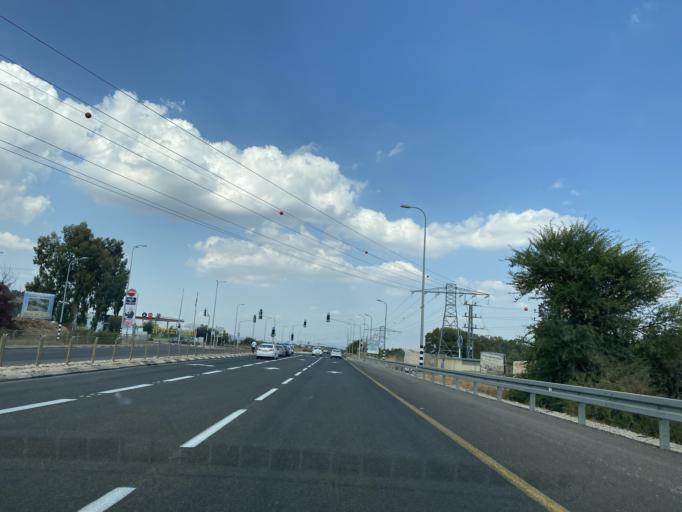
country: IL
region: Northern District
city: Rosh Pinna
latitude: 32.9809
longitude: 35.5574
